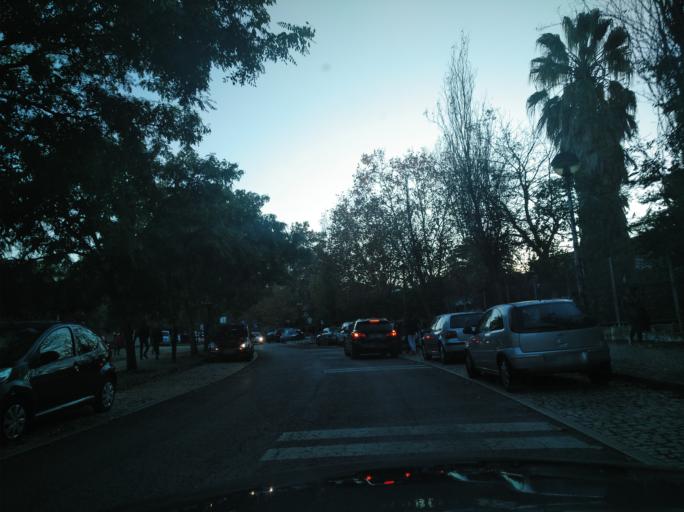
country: PT
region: Lisbon
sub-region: Odivelas
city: Olival do Basto
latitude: 38.7701
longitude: -9.1612
